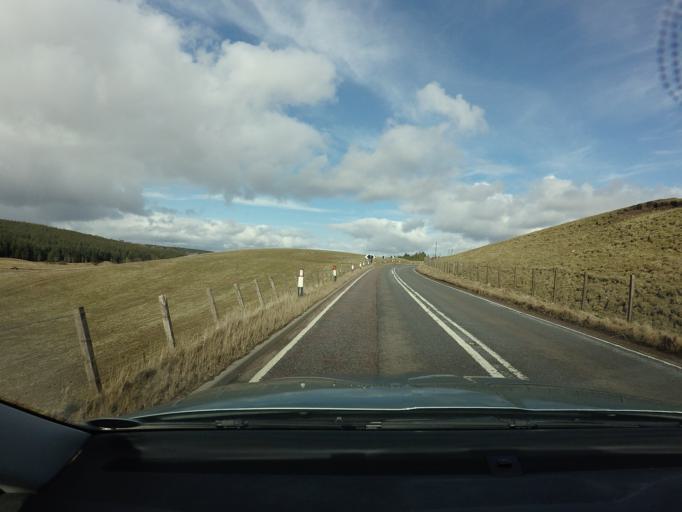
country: GB
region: Scotland
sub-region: South Lanarkshire
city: Douglas
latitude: 55.5413
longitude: -3.8663
